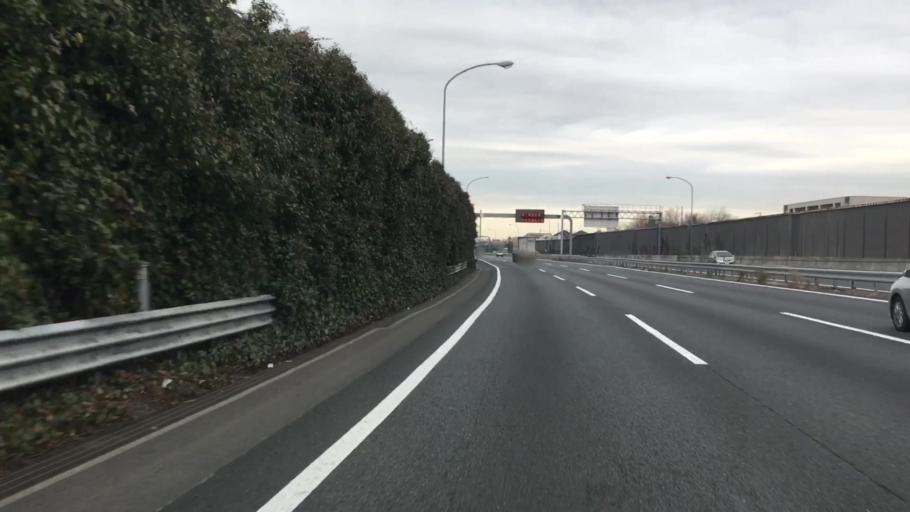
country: JP
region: Saitama
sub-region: Kawaguchi-shi
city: Hatogaya-honcho
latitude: 35.8758
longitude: 139.7336
